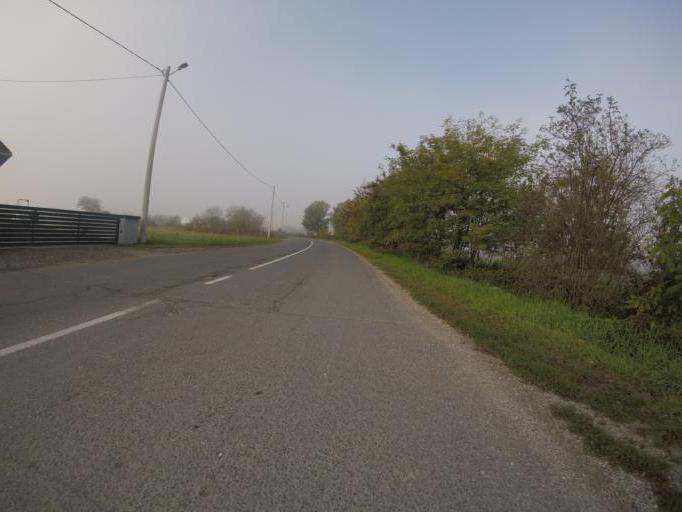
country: HR
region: Zagrebacka
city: Micevec
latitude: 45.7641
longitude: 16.0767
